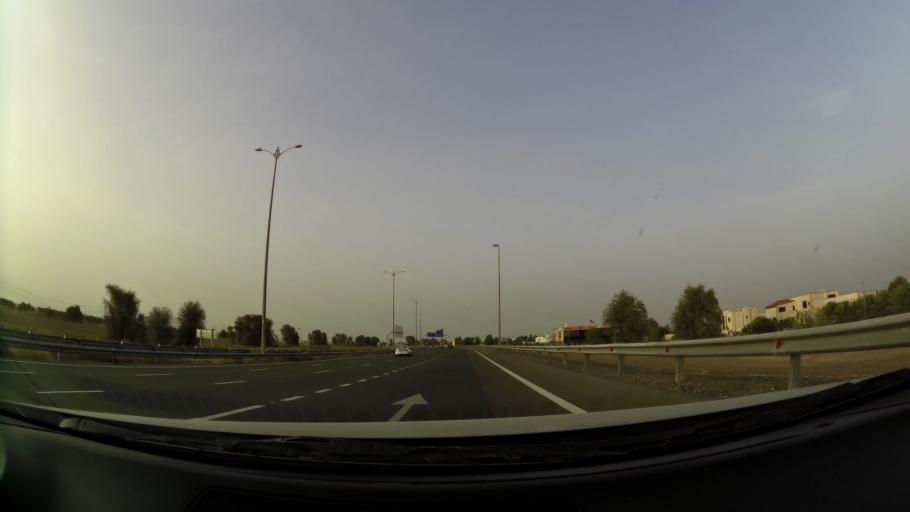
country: OM
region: Al Buraimi
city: Al Buraymi
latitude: 24.2794
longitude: 55.7292
